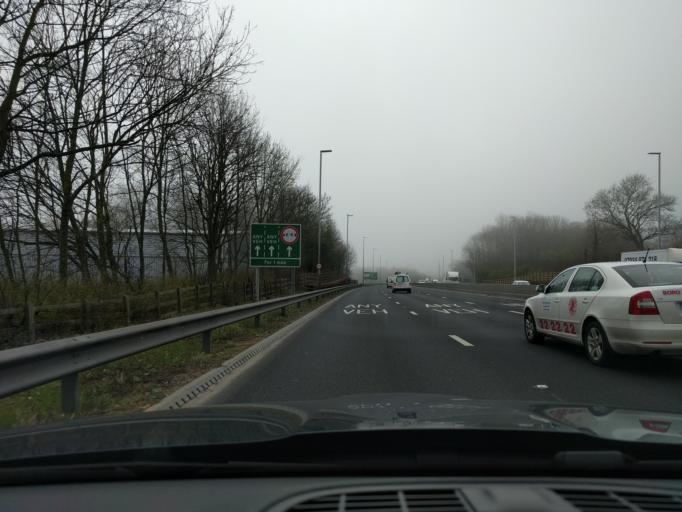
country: GB
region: England
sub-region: Gateshead
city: Lamesley
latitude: 54.9352
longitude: -1.6285
